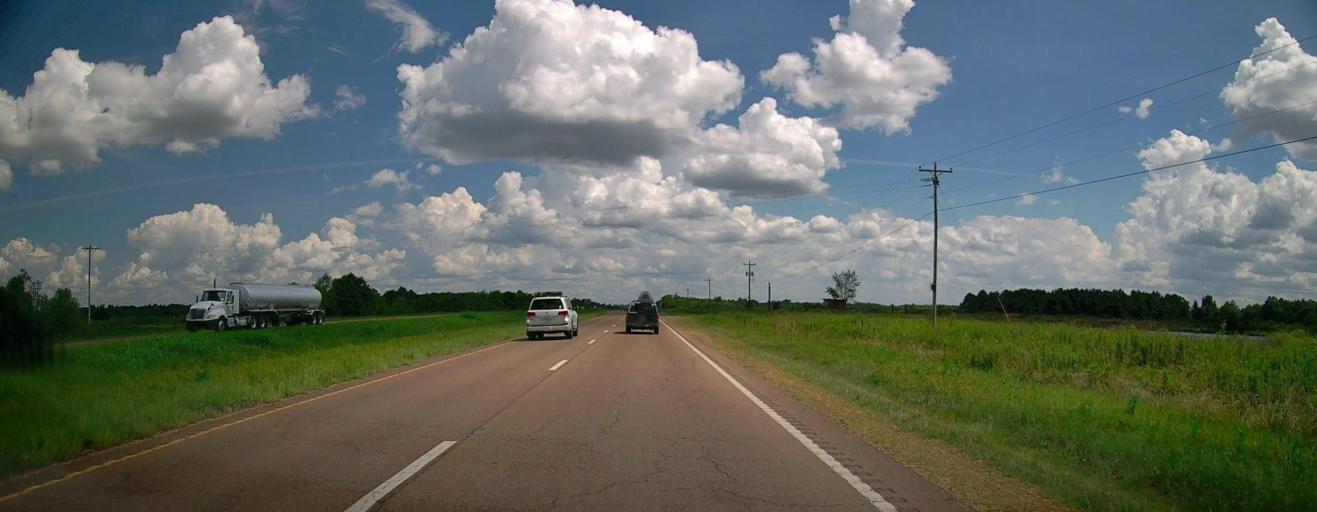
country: US
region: Mississippi
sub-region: Lowndes County
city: Columbus Air Force Base
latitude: 33.6951
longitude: -88.4415
